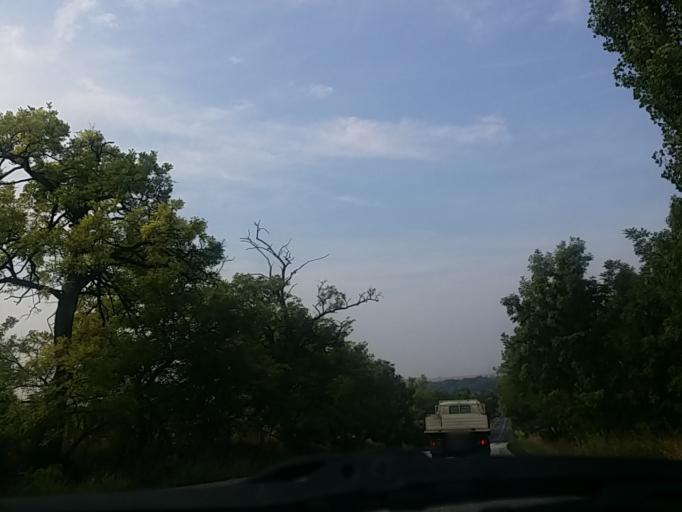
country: HU
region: Fejer
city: Bicske
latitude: 47.5101
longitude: 18.6411
